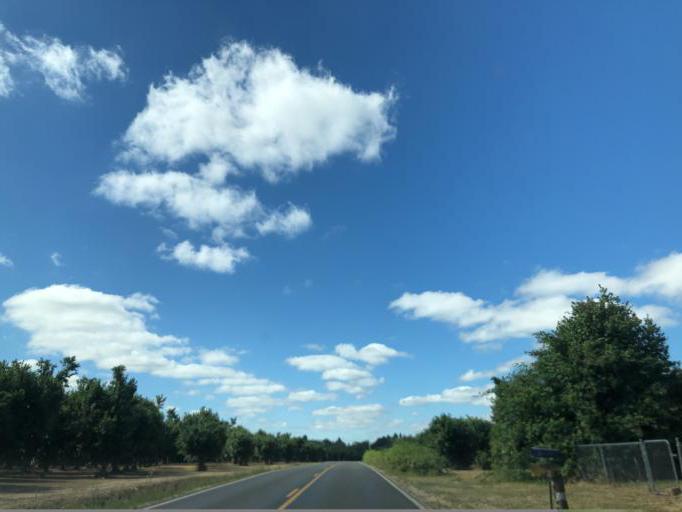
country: US
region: Oregon
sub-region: Marion County
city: Mount Angel
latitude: 45.1067
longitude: -122.7289
